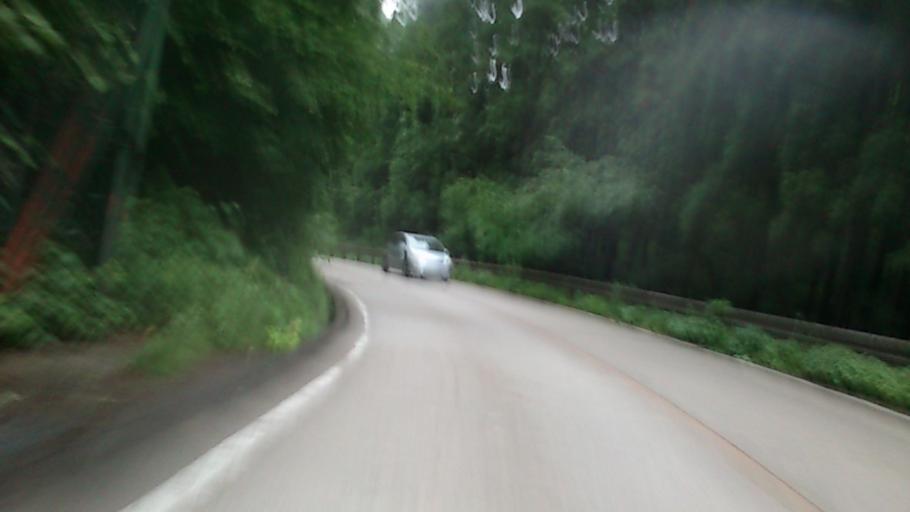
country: JP
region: Fukushima
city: Fukushima-shi
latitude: 37.7484
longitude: 140.3324
